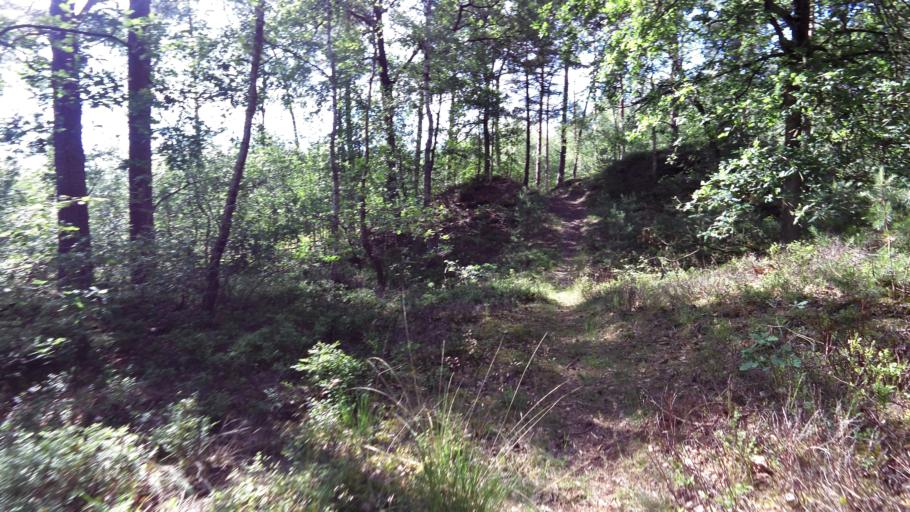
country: NL
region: Gelderland
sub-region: Gemeente Epe
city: Vaassen
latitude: 52.2684
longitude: 5.9282
